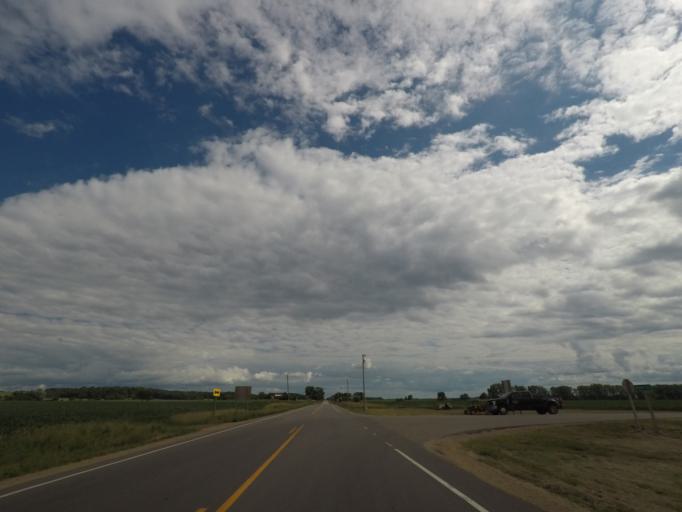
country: US
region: Wisconsin
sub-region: Green County
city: Albany
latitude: 42.7202
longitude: -89.3683
